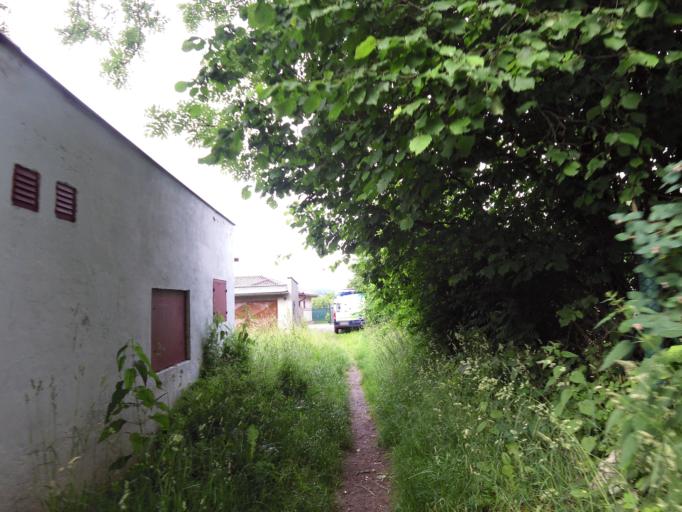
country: CZ
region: Ustecky
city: Varnsdorf
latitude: 50.9006
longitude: 14.6207
